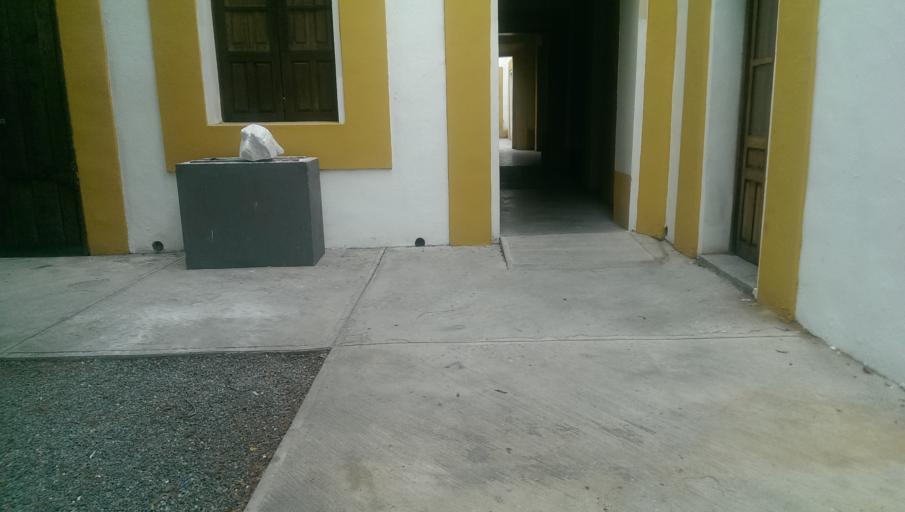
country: MX
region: Nuevo Leon
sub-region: Monterrey
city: Monterrey
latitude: 25.6654
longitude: -100.3065
